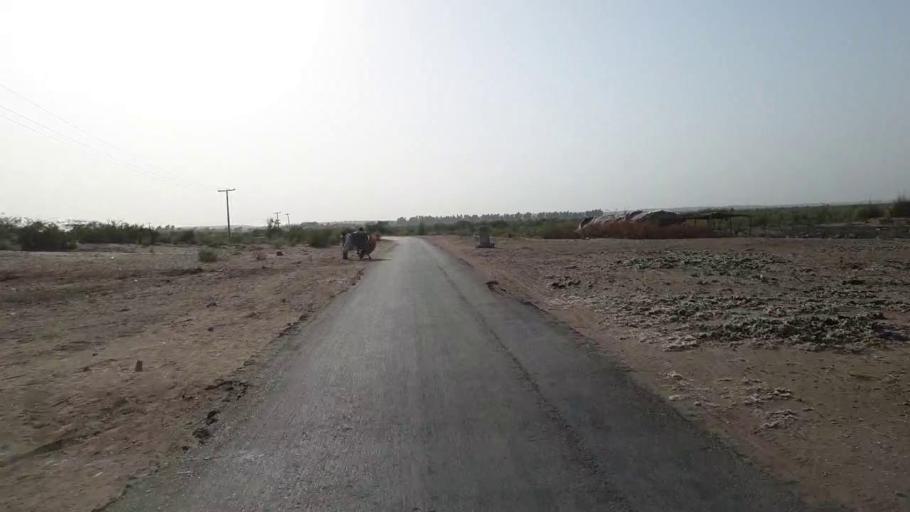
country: PK
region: Sindh
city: Jam Sahib
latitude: 26.4375
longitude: 68.8690
